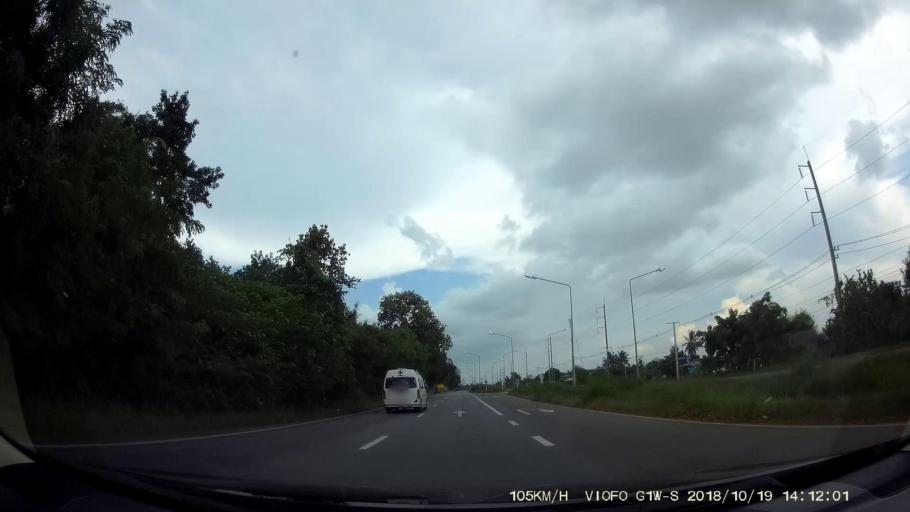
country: TH
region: Chaiyaphum
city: Khon Sawan
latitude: 15.9440
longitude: 102.1683
